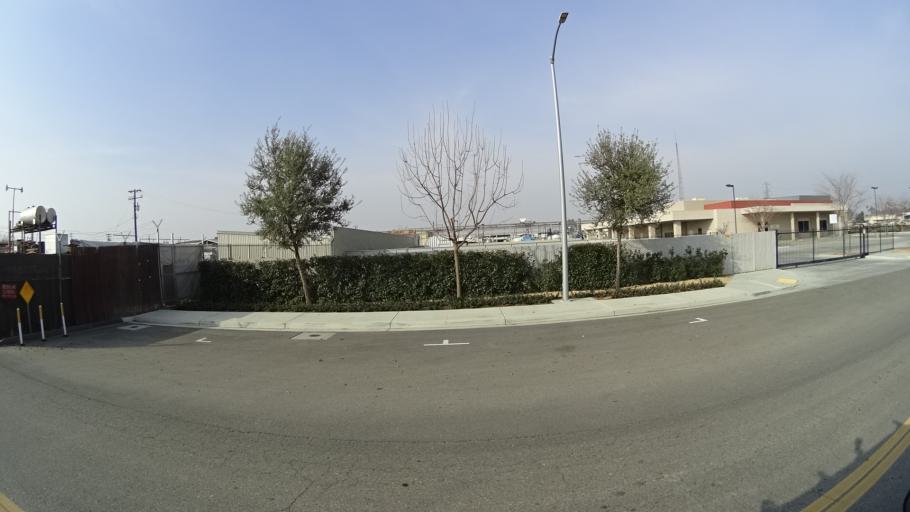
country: US
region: California
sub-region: Kern County
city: Bakersfield
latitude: 35.3951
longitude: -119.0387
